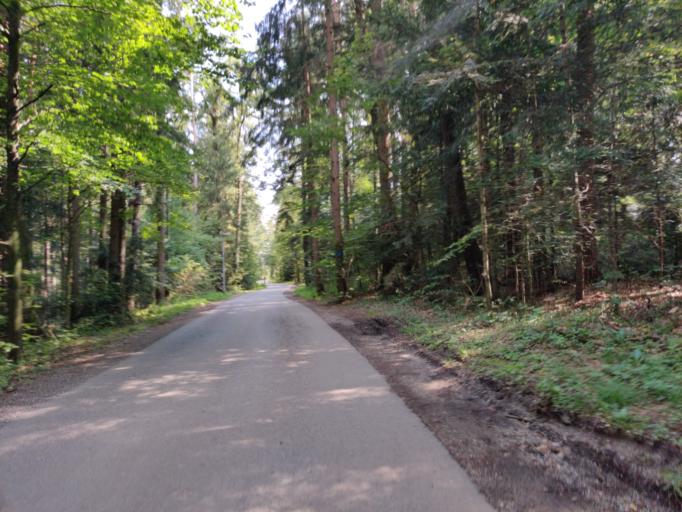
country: AT
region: Styria
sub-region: Graz Stadt
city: Mariatrost
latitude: 47.1275
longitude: 15.5050
